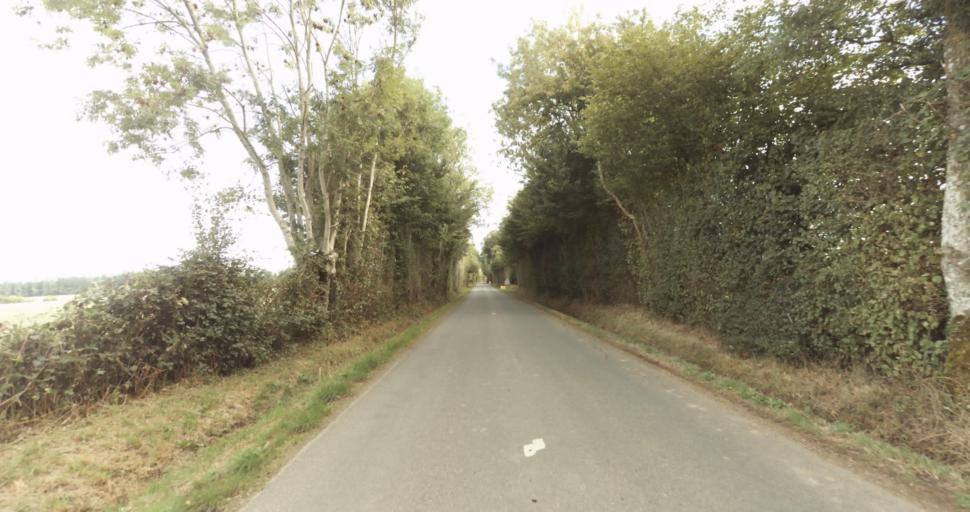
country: FR
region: Lower Normandy
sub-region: Departement de l'Orne
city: Gace
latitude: 48.8419
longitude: 0.2473
